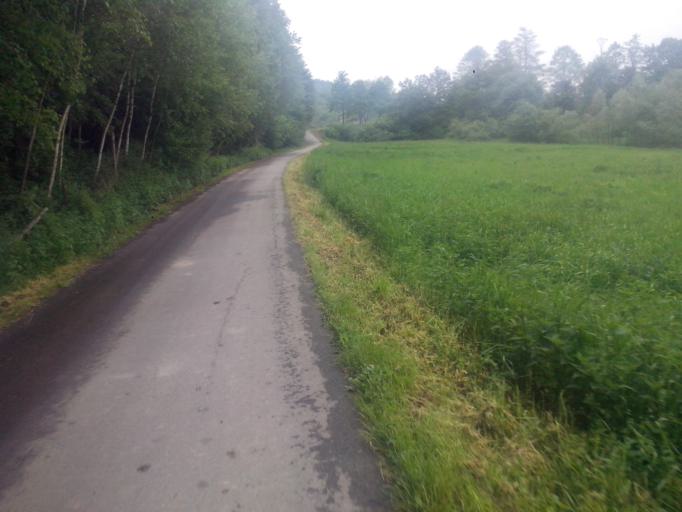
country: PL
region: Subcarpathian Voivodeship
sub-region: Powiat strzyzowski
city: Strzyzow
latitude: 49.8701
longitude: 21.8147
